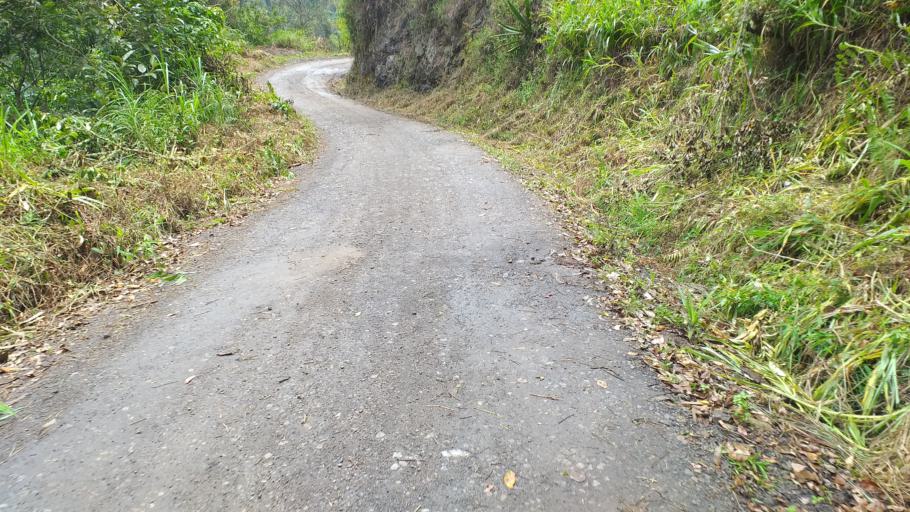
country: CO
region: Cundinamarca
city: Tenza
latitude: 5.1137
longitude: -73.4528
